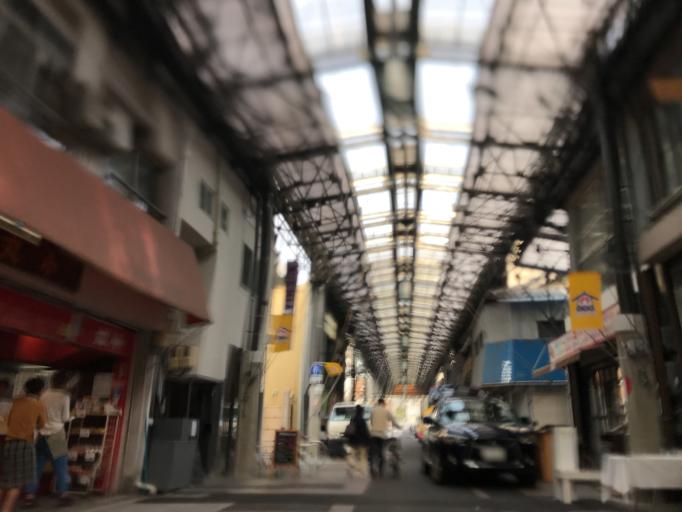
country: JP
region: Aichi
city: Nagoya-shi
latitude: 35.1763
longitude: 136.8912
